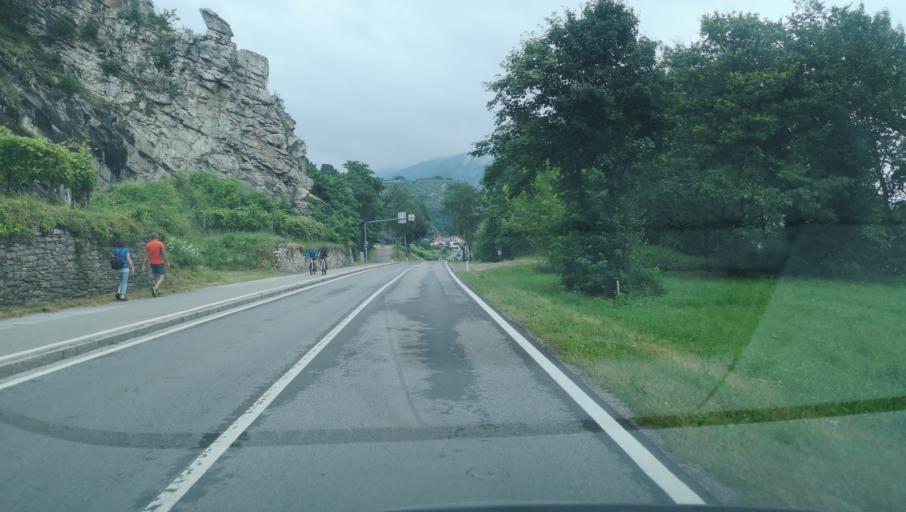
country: AT
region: Lower Austria
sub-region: Politischer Bezirk Krems
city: Spitz
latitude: 48.3529
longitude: 15.4065
